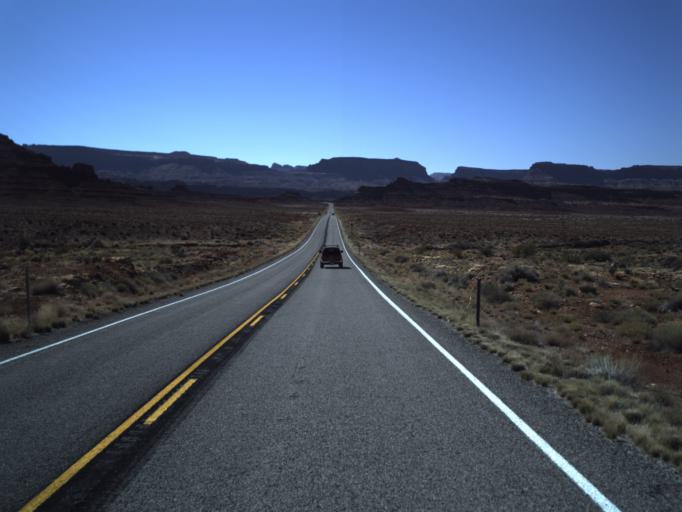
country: US
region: Utah
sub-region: San Juan County
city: Blanding
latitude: 37.8497
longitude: -110.3541
